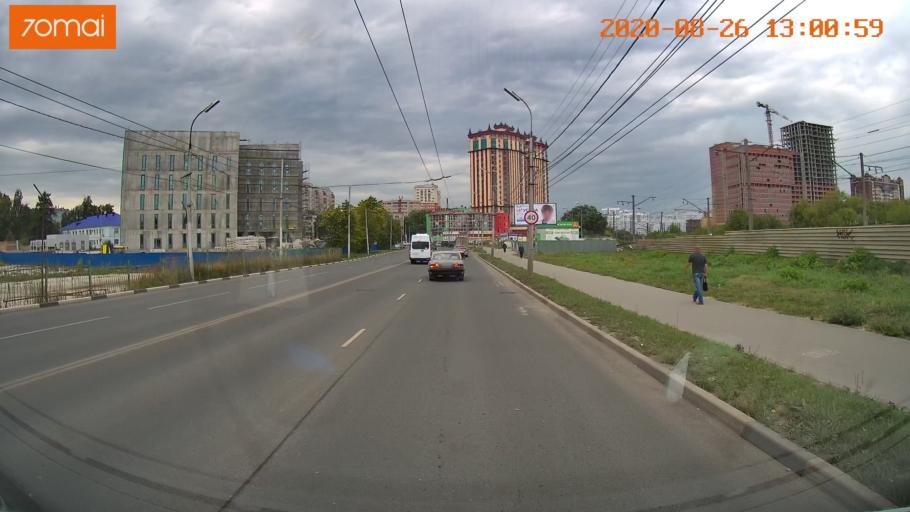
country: RU
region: Rjazan
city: Ryazan'
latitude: 54.6172
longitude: 39.7375
